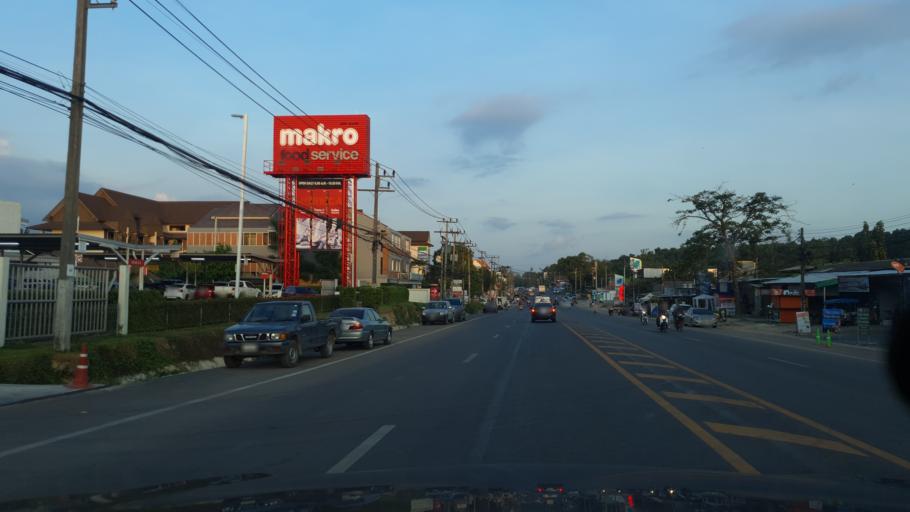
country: TH
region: Phangnga
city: Ban Ao Nang
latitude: 8.0417
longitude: 98.8404
